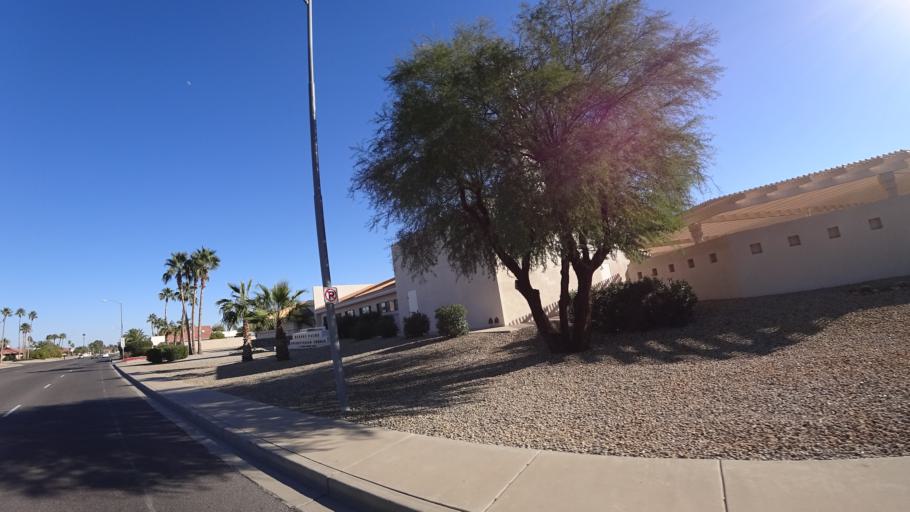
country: US
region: Arizona
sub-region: Maricopa County
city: Sun City West
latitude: 33.6787
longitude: -112.3538
